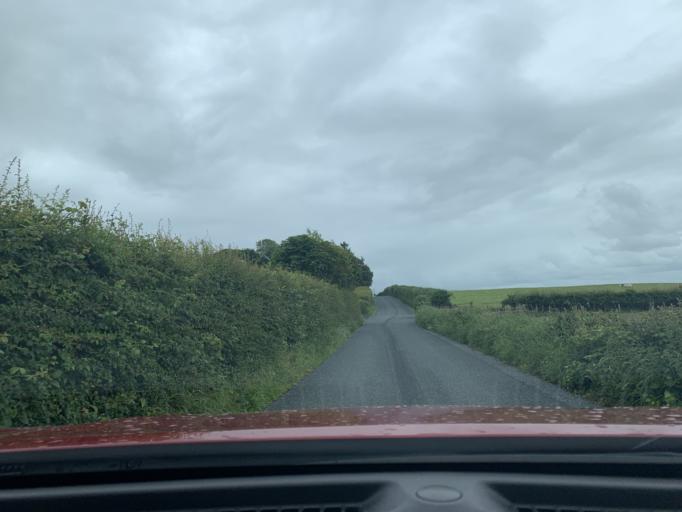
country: IE
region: Connaught
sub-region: Sligo
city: Sligo
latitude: 54.3105
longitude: -8.4749
